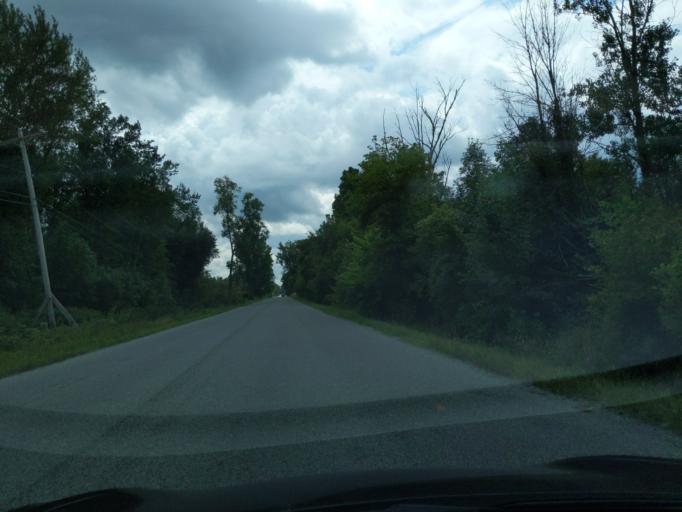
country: US
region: Michigan
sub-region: Eaton County
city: Dimondale
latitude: 42.6477
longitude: -84.5825
